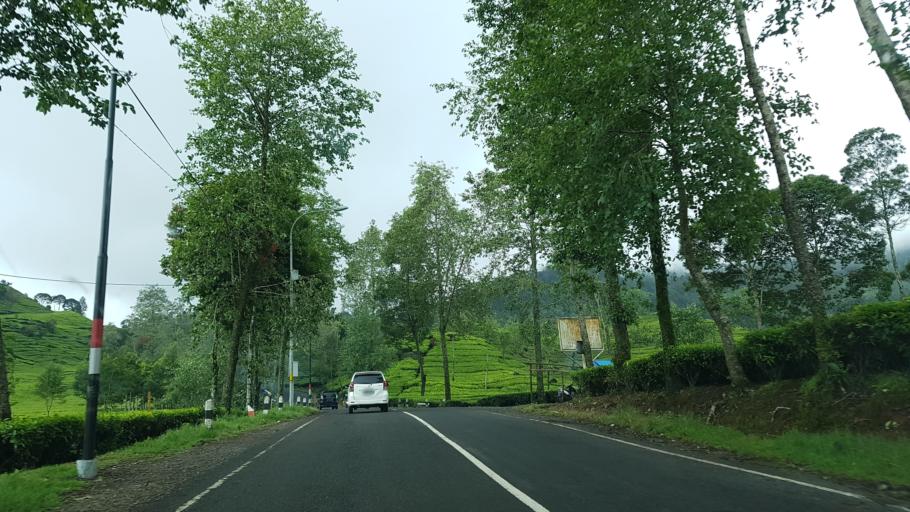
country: ID
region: West Java
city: Banjar
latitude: -7.1509
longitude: 107.3762
